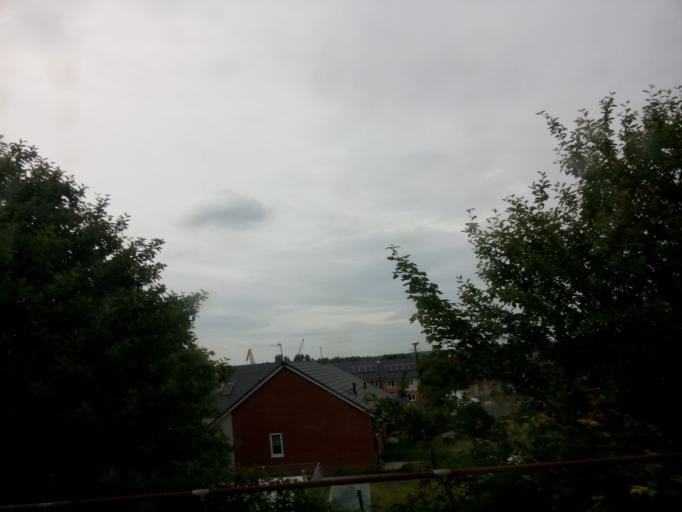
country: GB
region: England
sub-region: South Tyneside
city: Hebburn
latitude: 54.9807
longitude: -1.5073
